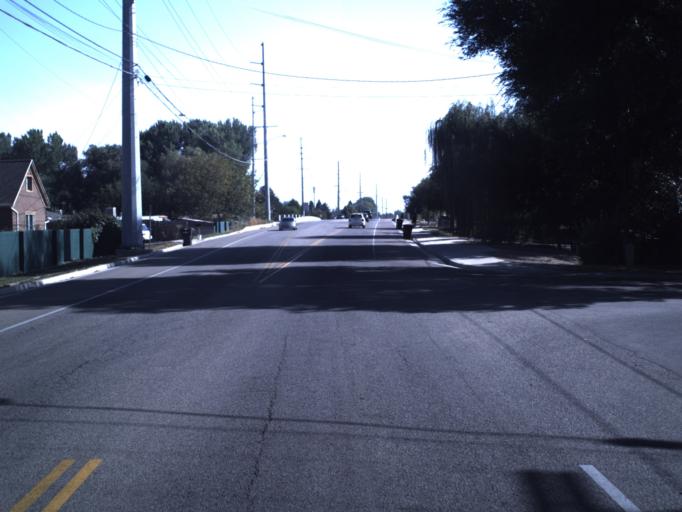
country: US
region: Utah
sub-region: Utah County
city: Provo
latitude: 40.2397
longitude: -111.6949
